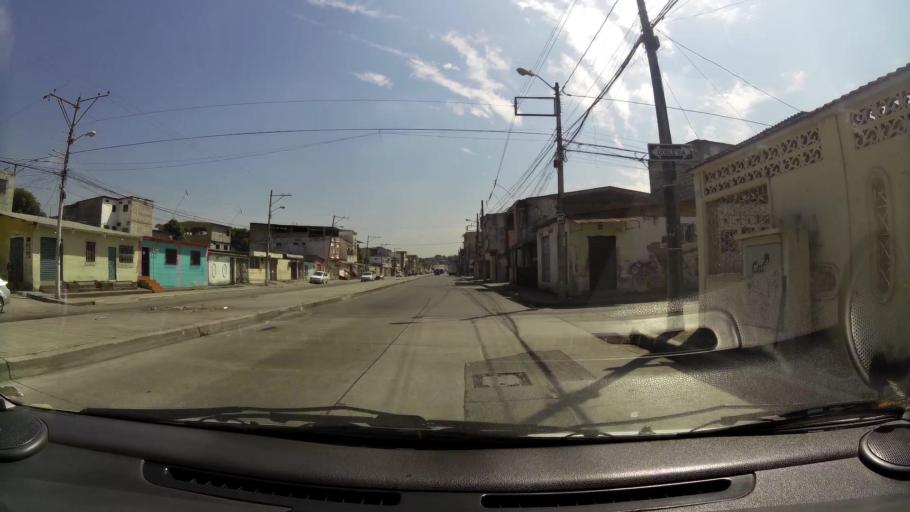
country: EC
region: Guayas
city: Eloy Alfaro
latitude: -2.1283
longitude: -79.9118
